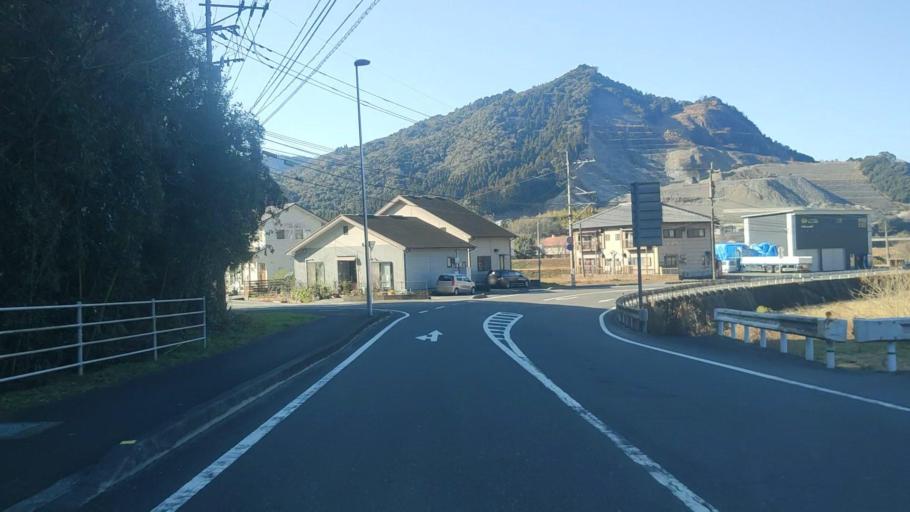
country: JP
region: Oita
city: Saiki
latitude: 32.9769
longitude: 131.8524
